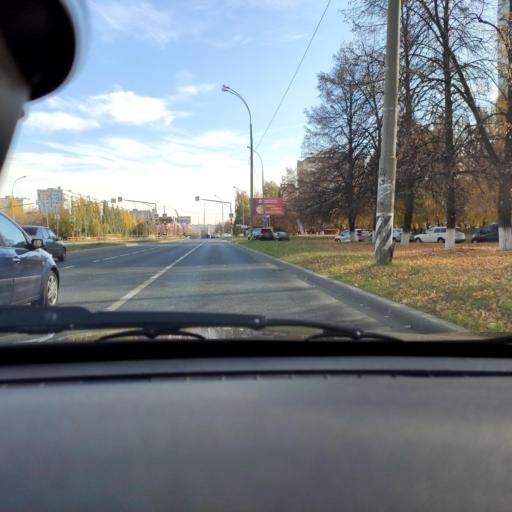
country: RU
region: Samara
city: Tol'yatti
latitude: 53.5264
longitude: 49.3080
